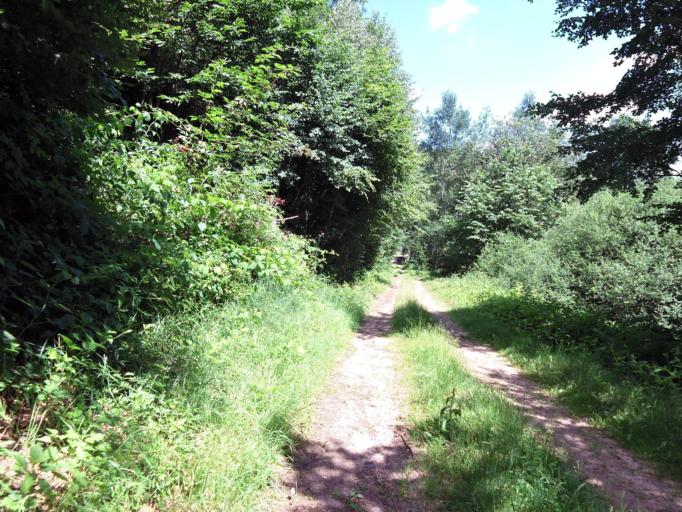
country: DE
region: Rheinland-Pfalz
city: Trippstadt
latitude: 49.3368
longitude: 7.8285
